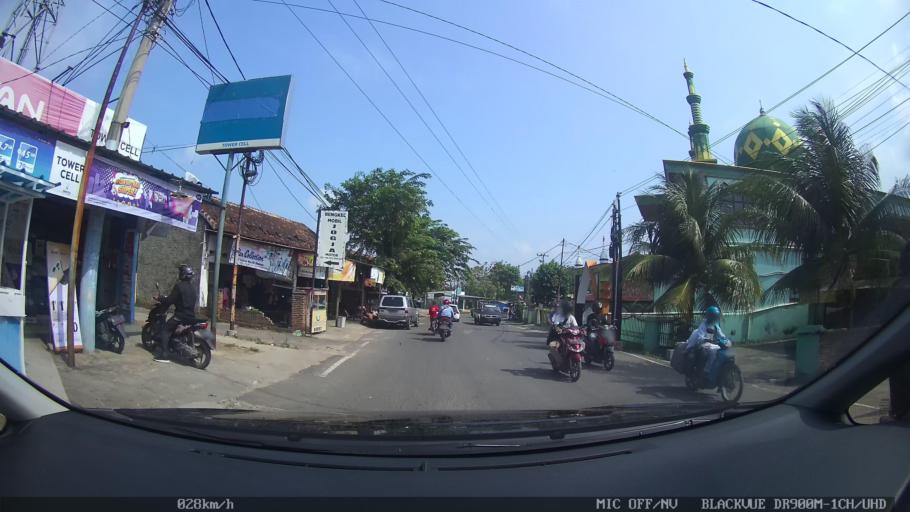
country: ID
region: Lampung
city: Kedaton
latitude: -5.3644
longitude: 105.2564
